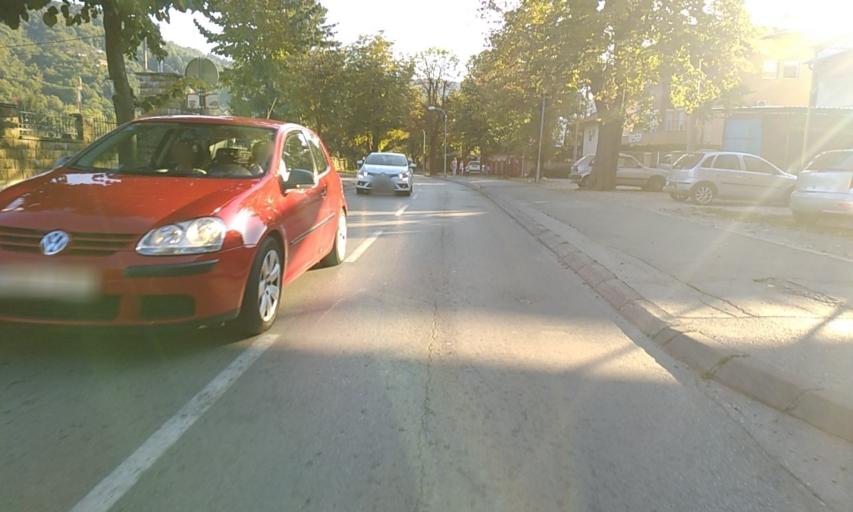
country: BA
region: Republika Srpska
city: Hiseti
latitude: 44.7592
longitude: 17.1841
